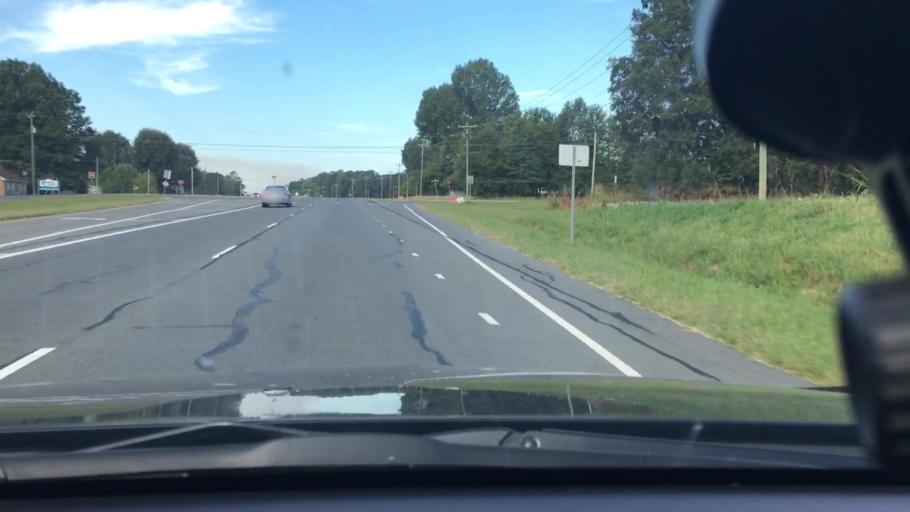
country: US
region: North Carolina
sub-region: Stanly County
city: Oakboro
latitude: 35.2687
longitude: -80.3616
